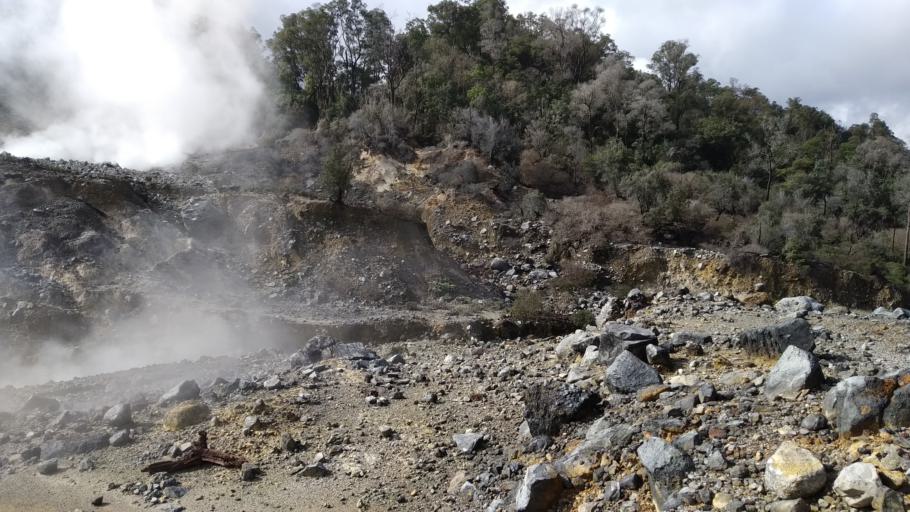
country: ID
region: West Java
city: Cicurug
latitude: -6.7170
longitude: 106.7128
